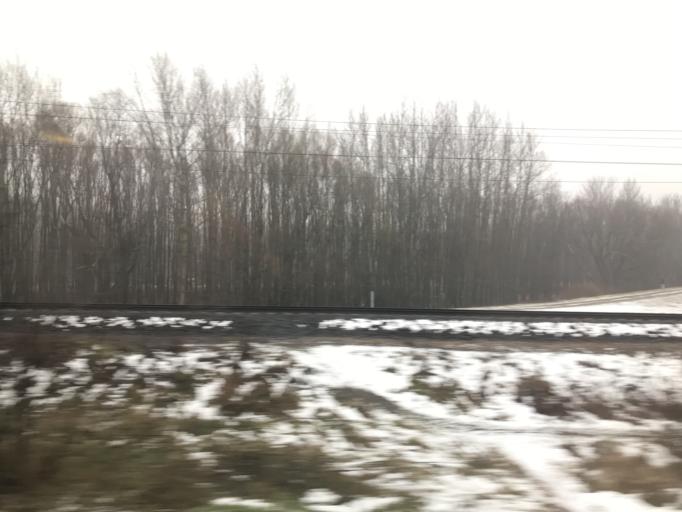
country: HU
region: Gyor-Moson-Sopron
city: Gyor
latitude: 47.6766
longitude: 17.6132
